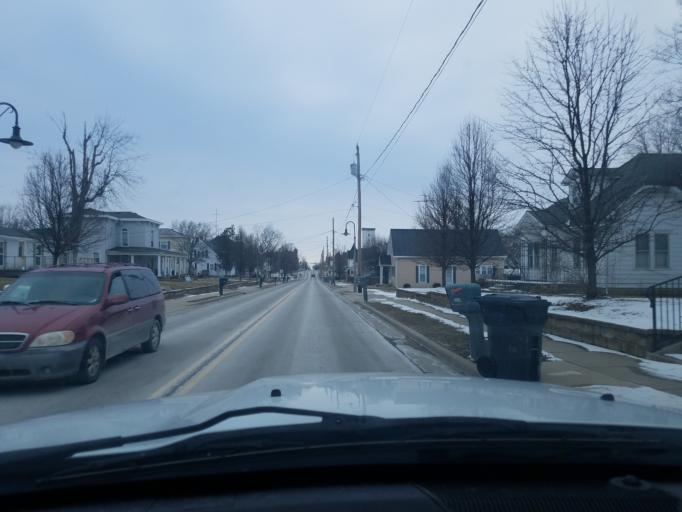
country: US
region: Indiana
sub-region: Randolph County
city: Farmland
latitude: 40.1841
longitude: -85.1277
